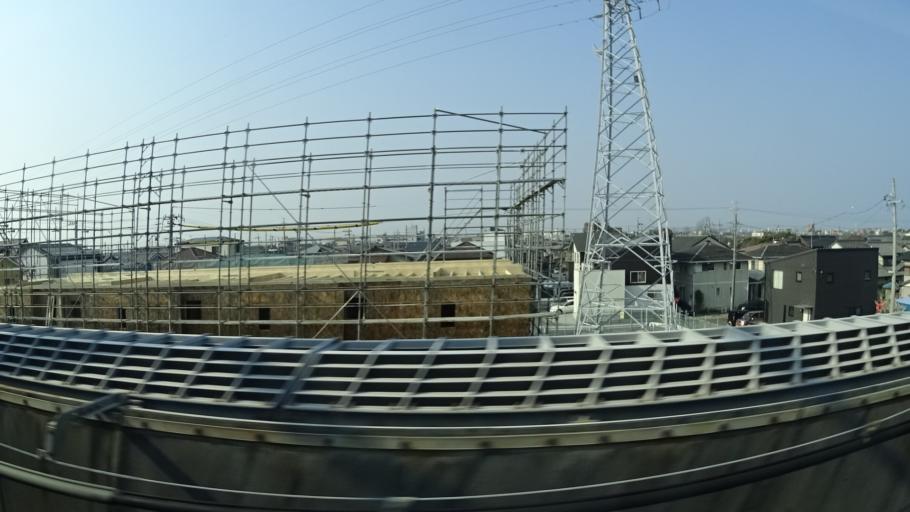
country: JP
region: Aichi
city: Toyohashi
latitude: 34.7396
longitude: 137.4035
